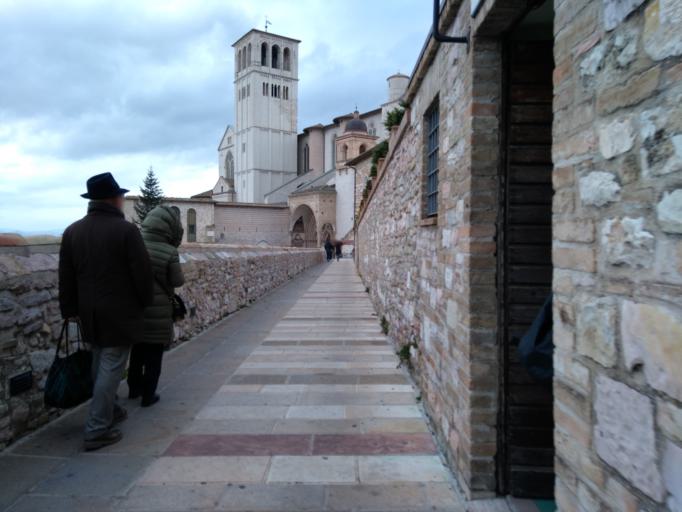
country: IT
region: Umbria
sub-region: Provincia di Perugia
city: Assisi
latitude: 43.0740
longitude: 12.6069
